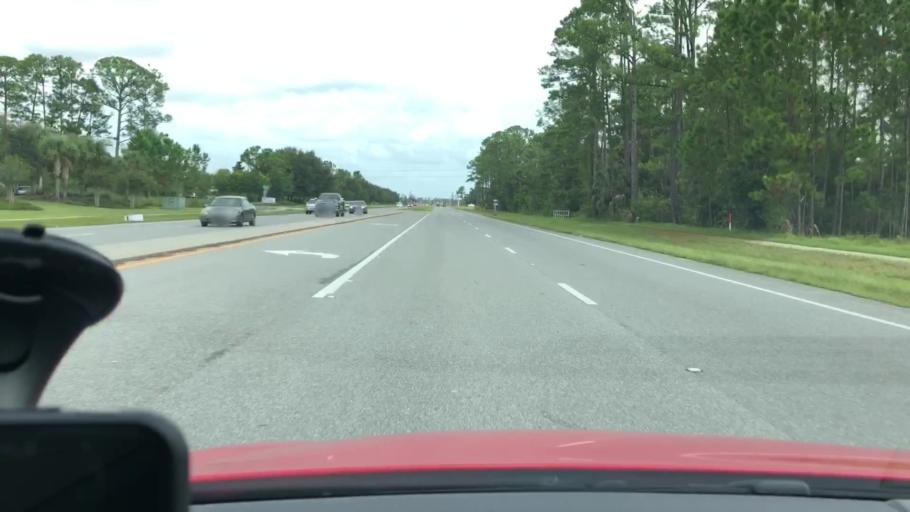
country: US
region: Florida
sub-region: Volusia County
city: Holly Hill
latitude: 29.2077
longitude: -81.0888
